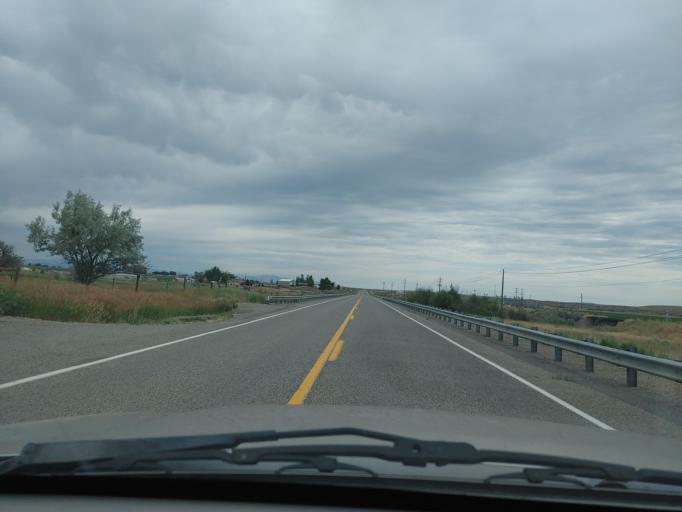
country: US
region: Idaho
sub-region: Lincoln County
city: Shoshone
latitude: 43.0510
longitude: -114.1410
